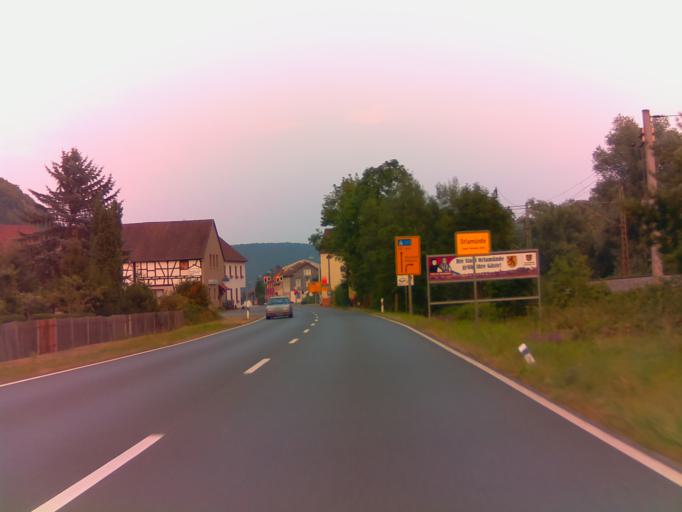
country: DE
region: Thuringia
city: Orlamunde
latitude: 50.7750
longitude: 11.5290
